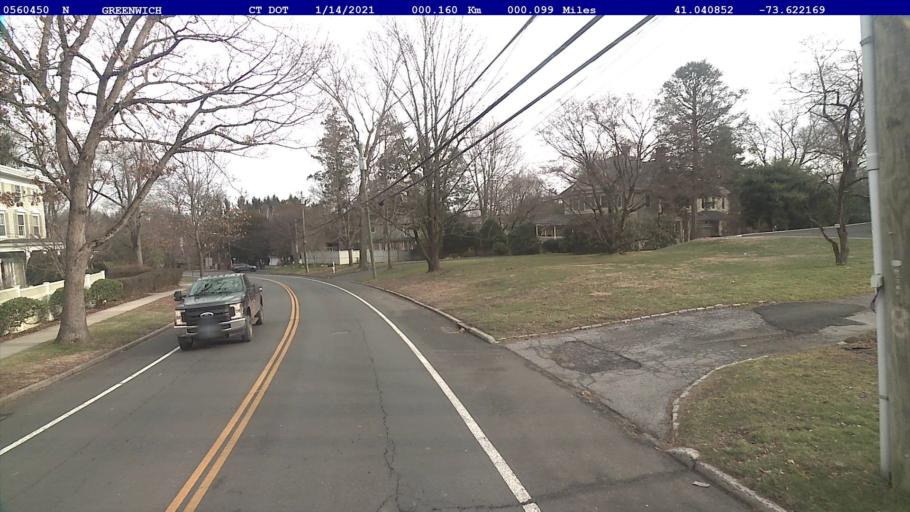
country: US
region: Connecticut
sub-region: Fairfield County
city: Greenwich
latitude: 41.0409
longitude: -73.6222
